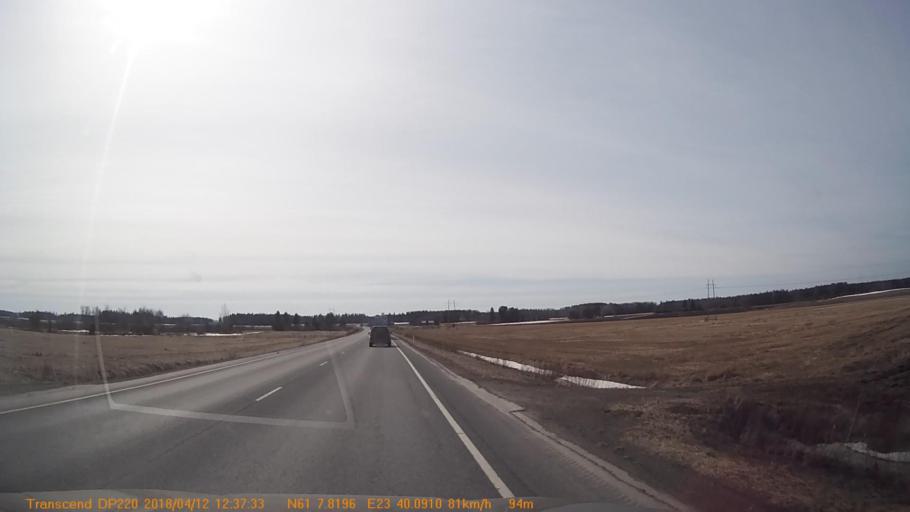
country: FI
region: Pirkanmaa
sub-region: Etelae-Pirkanmaa
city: Kylmaekoski
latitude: 61.1305
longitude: 23.6686
